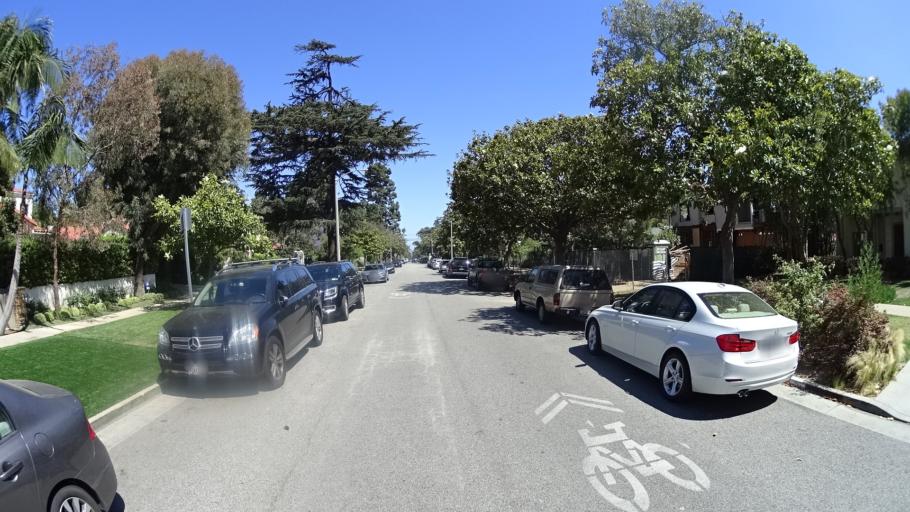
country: US
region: California
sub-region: Los Angeles County
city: Santa Monica
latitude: 34.0364
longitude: -118.4945
